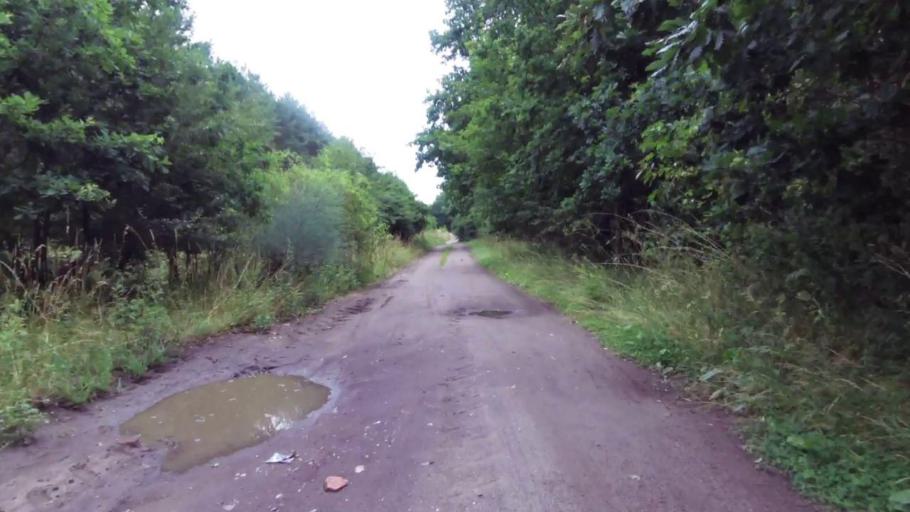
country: PL
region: West Pomeranian Voivodeship
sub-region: Powiat pyrzycki
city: Lipiany
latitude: 52.9748
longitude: 14.9117
